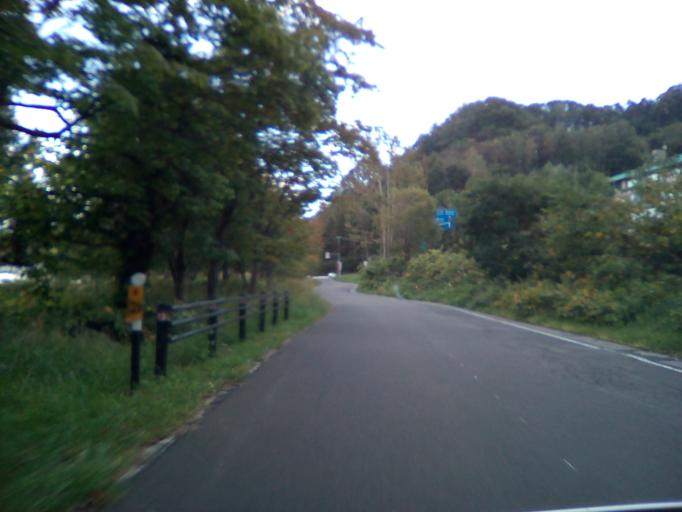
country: JP
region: Hokkaido
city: Date
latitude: 42.5800
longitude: 140.7963
